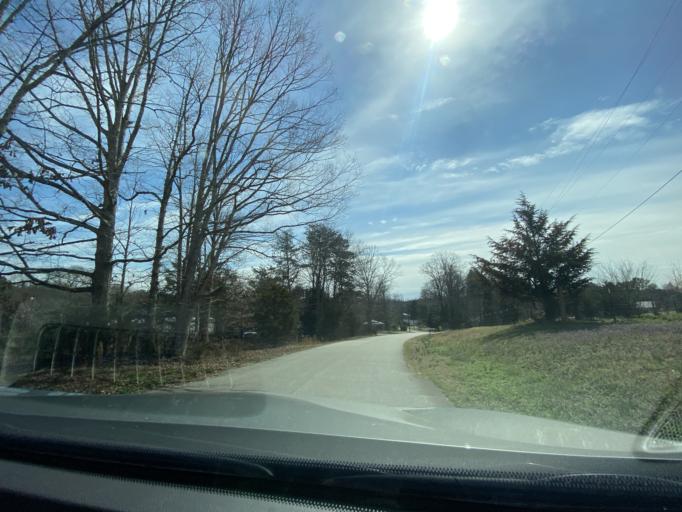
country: US
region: South Carolina
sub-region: Pickens County
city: Liberty
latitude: 34.8307
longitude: -82.7135
